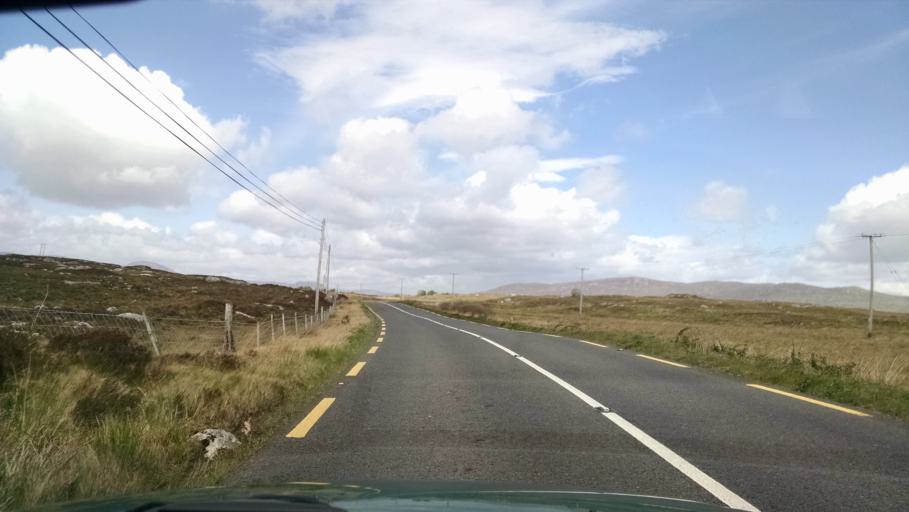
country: IE
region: Connaught
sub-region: County Galway
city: Oughterard
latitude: 53.3494
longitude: -9.5422
